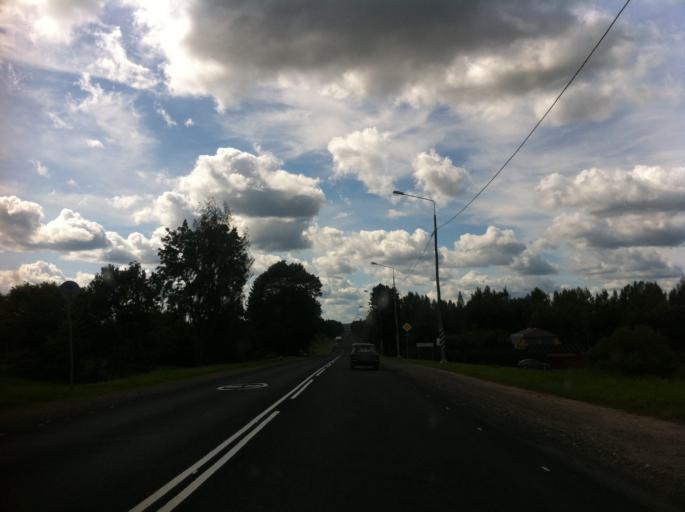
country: RU
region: Pskov
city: Izborsk
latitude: 57.7175
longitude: 27.9224
